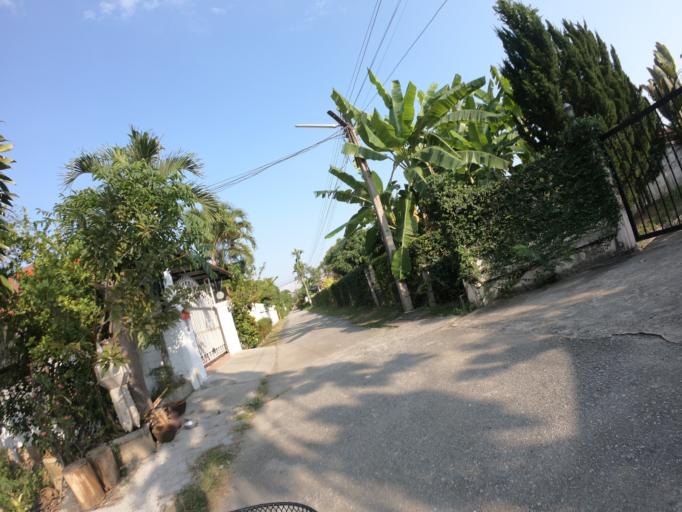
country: TH
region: Chiang Mai
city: Chiang Mai
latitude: 18.8333
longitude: 98.9848
